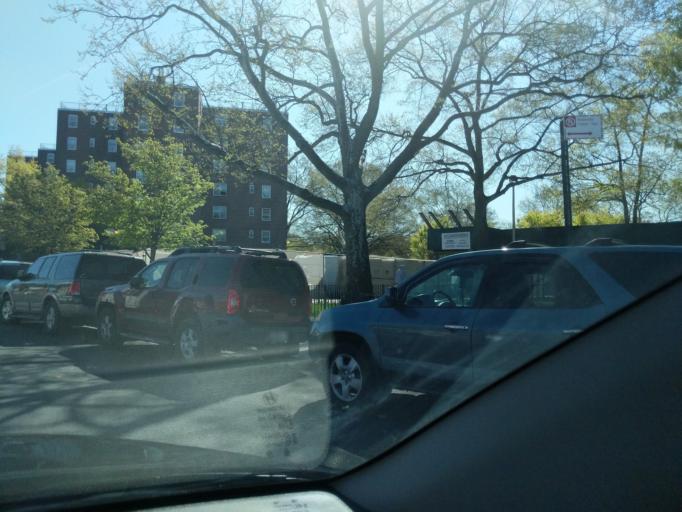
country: US
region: New York
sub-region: Kings County
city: East New York
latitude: 40.6483
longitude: -73.8975
